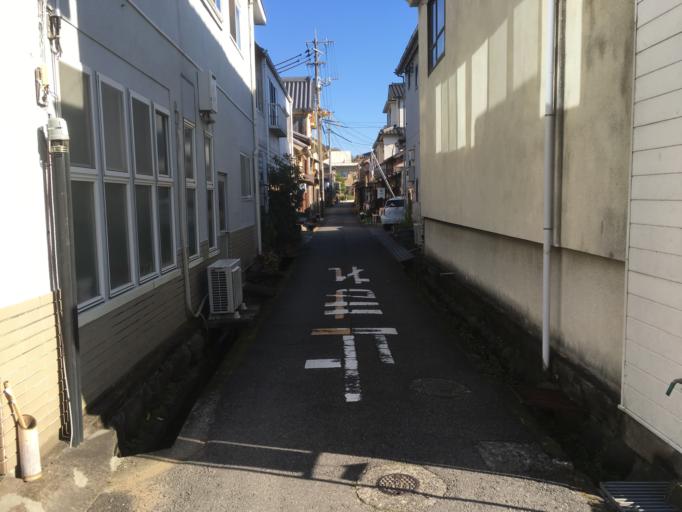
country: JP
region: Oita
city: Hita
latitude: 33.3285
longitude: 130.9362
